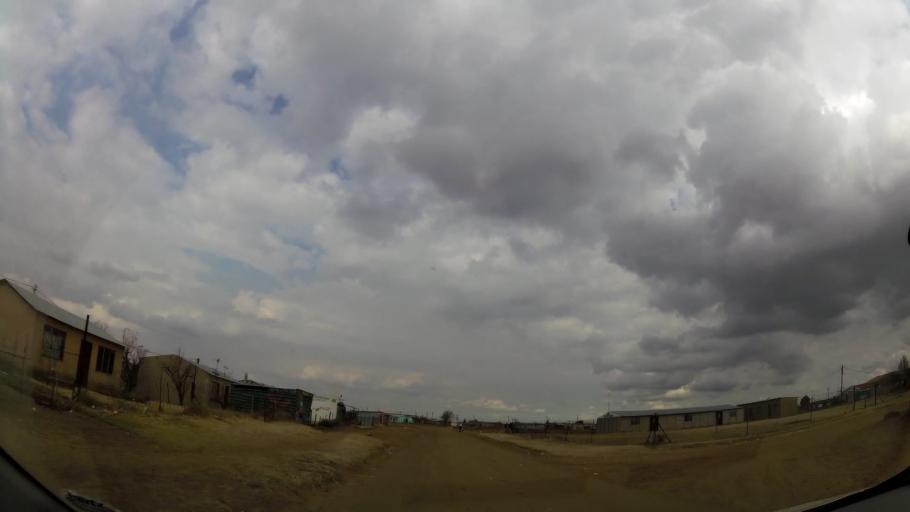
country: ZA
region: Orange Free State
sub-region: Fezile Dabi District Municipality
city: Sasolburg
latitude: -26.8649
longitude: 27.8664
